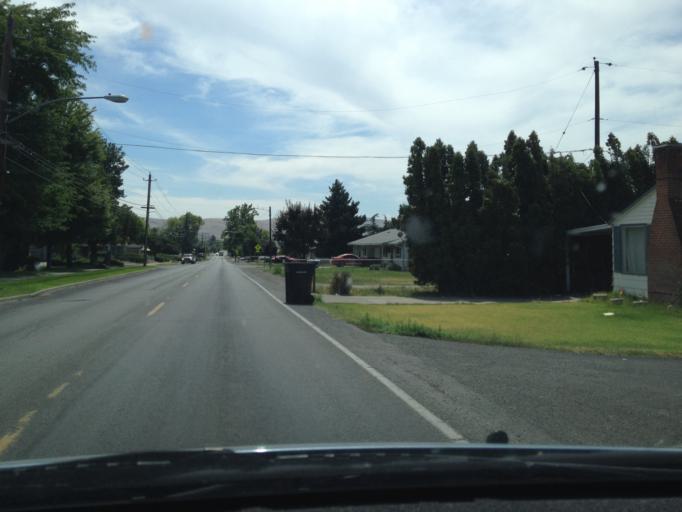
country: US
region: Washington
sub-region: Yakima County
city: West Valley
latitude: 46.5908
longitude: -120.5723
